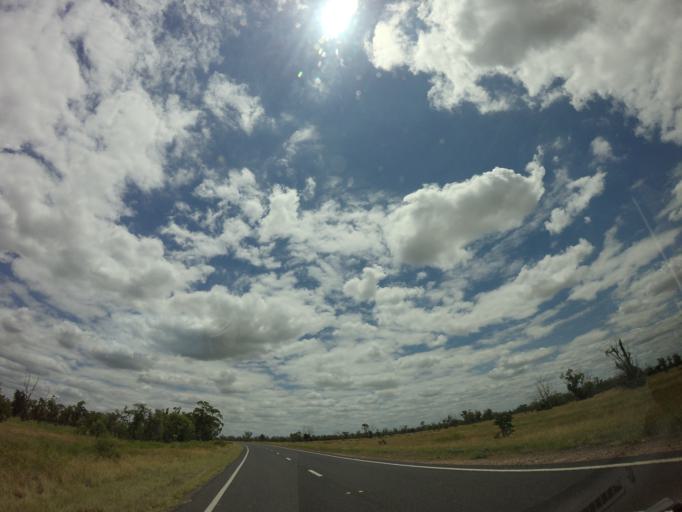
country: AU
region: New South Wales
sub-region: Moree Plains
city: Boggabilla
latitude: -28.6459
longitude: 150.3421
